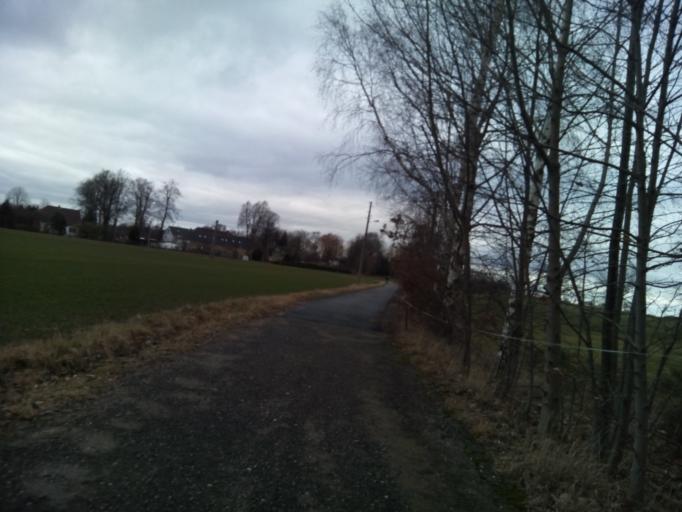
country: DE
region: Saxony
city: Freiberg
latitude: 50.8896
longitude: 13.3337
